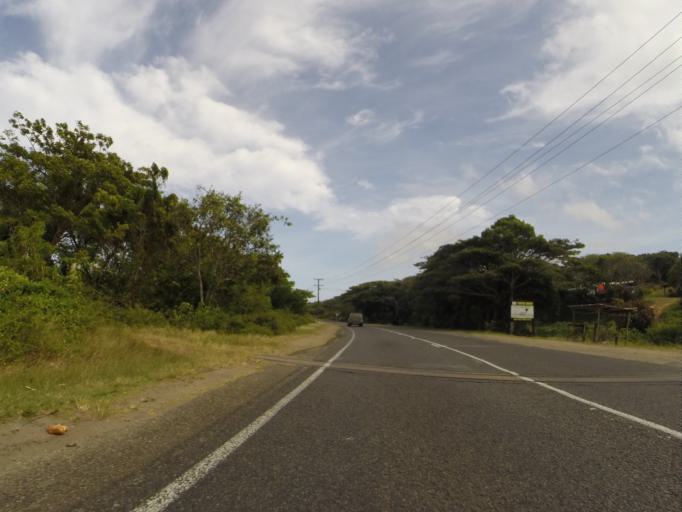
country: FJ
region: Western
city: Nadi
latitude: -18.1505
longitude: 177.4427
